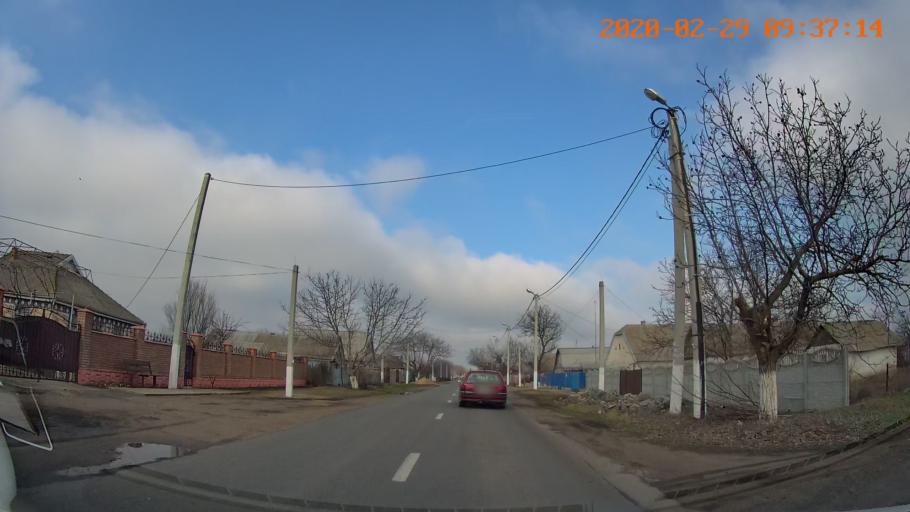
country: MD
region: Telenesti
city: Dnestrovsc
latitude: 46.6272
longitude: 29.8784
